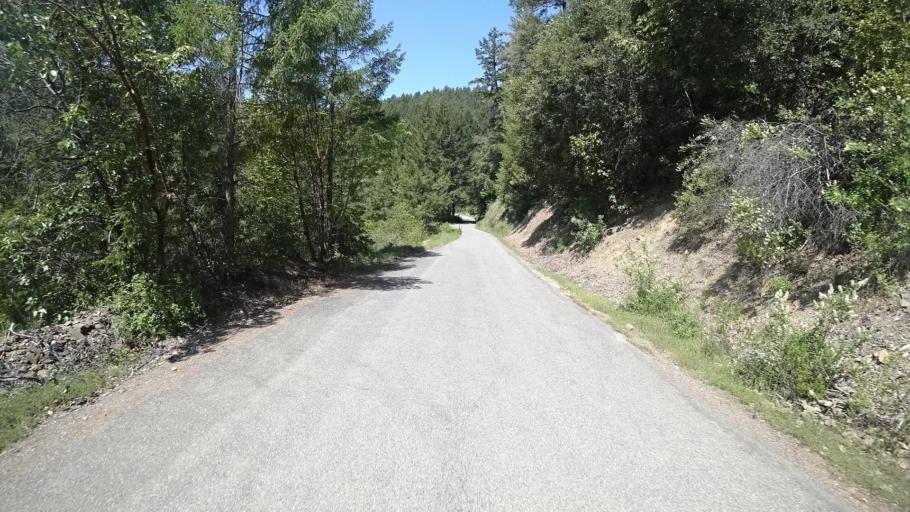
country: US
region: California
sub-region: Humboldt County
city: Redway
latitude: 40.1959
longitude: -123.5553
